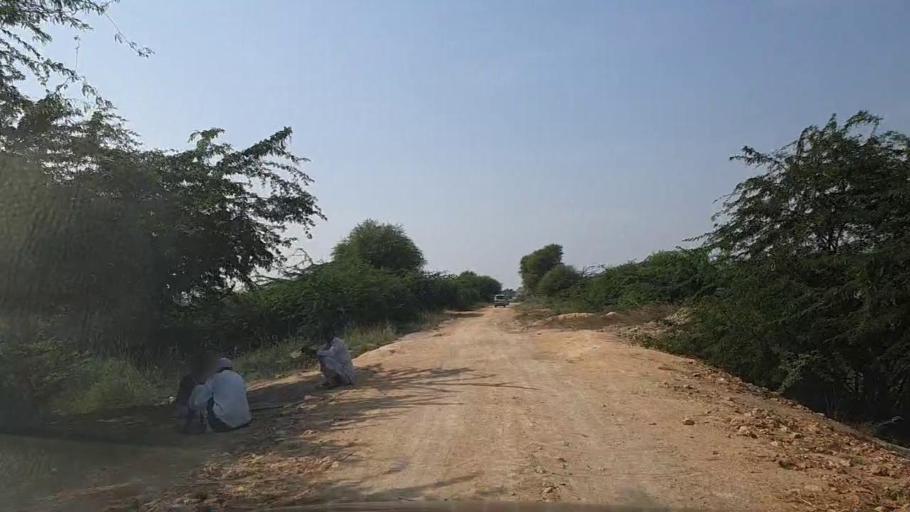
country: PK
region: Sindh
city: Thatta
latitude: 24.8066
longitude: 67.8681
